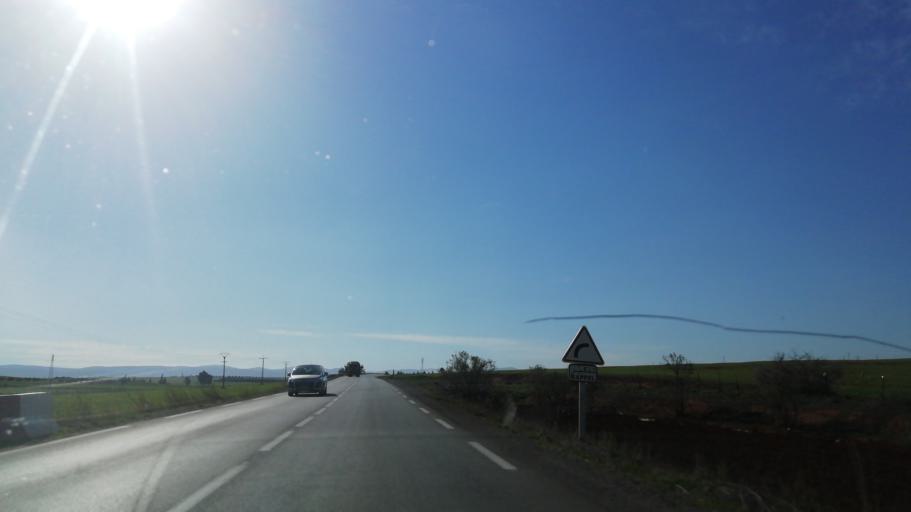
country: DZ
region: Tlemcen
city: Ouled Mimoun
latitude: 35.0006
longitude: -0.9074
